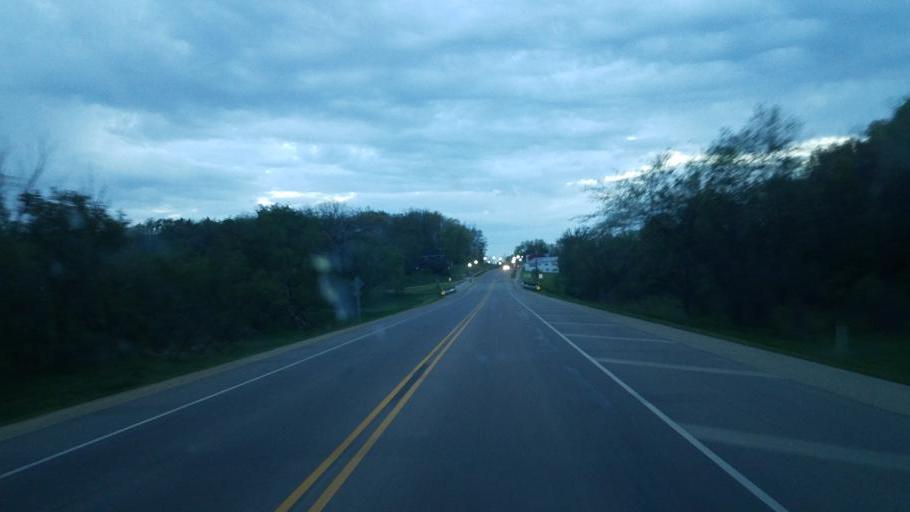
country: US
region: Wisconsin
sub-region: Juneau County
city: Elroy
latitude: 43.7321
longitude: -90.2673
